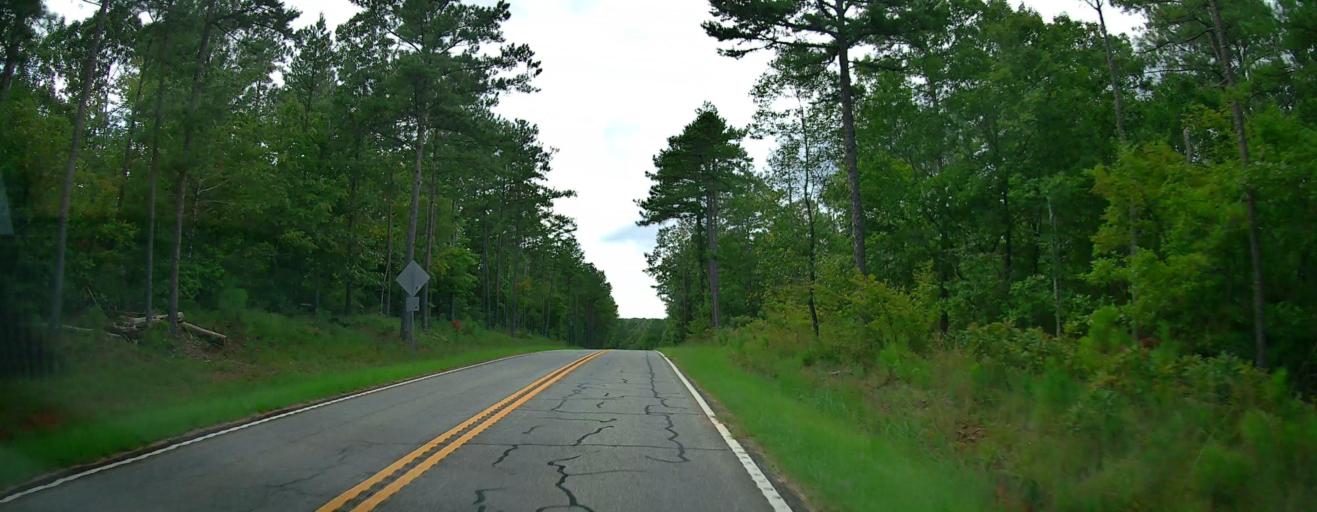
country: US
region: Georgia
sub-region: Meriwether County
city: Manchester
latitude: 32.8634
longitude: -84.7204
